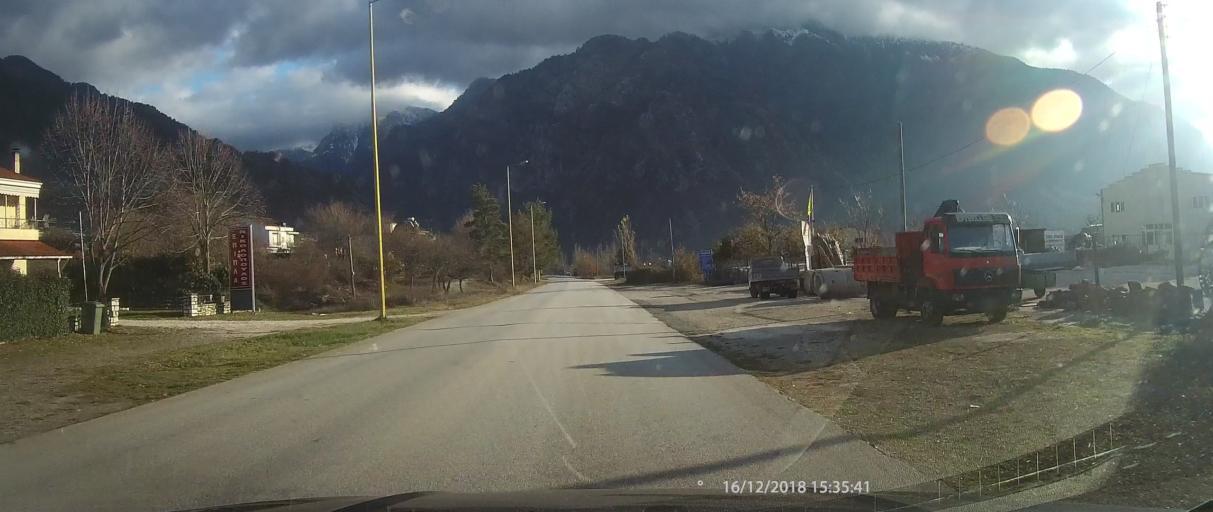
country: GR
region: Epirus
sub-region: Nomos Ioanninon
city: Konitsa
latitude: 40.0481
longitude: 20.7385
